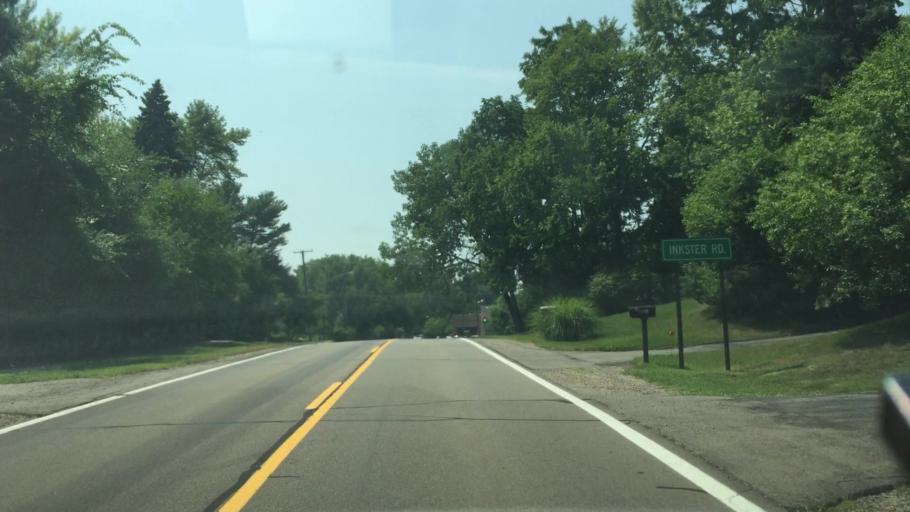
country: US
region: Michigan
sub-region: Oakland County
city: Franklin
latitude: 42.5514
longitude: -83.3195
